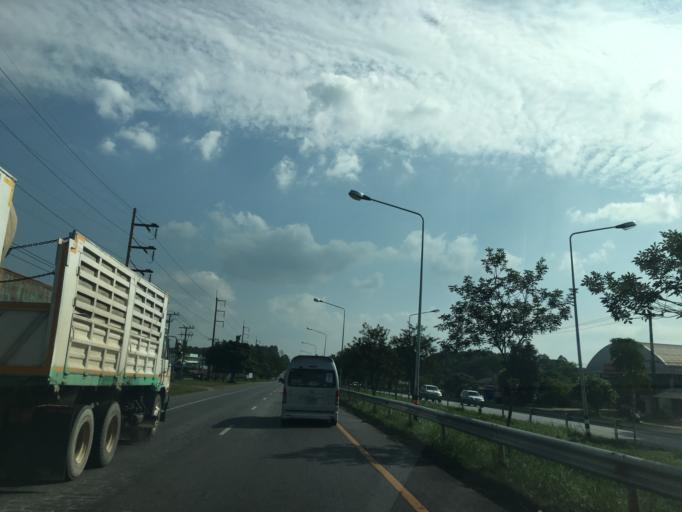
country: TH
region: Chiang Rai
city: Mae Lao
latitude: 19.7032
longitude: 99.7192
